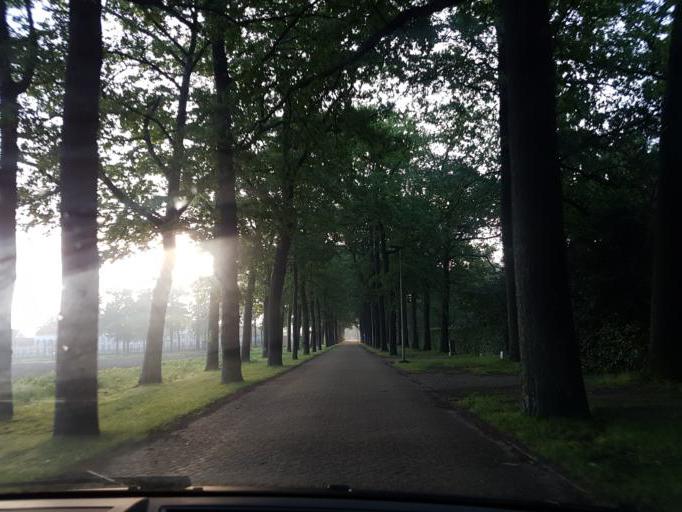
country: BE
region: Flanders
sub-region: Provincie Antwerpen
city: Merksplas
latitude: 51.3976
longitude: 4.8234
